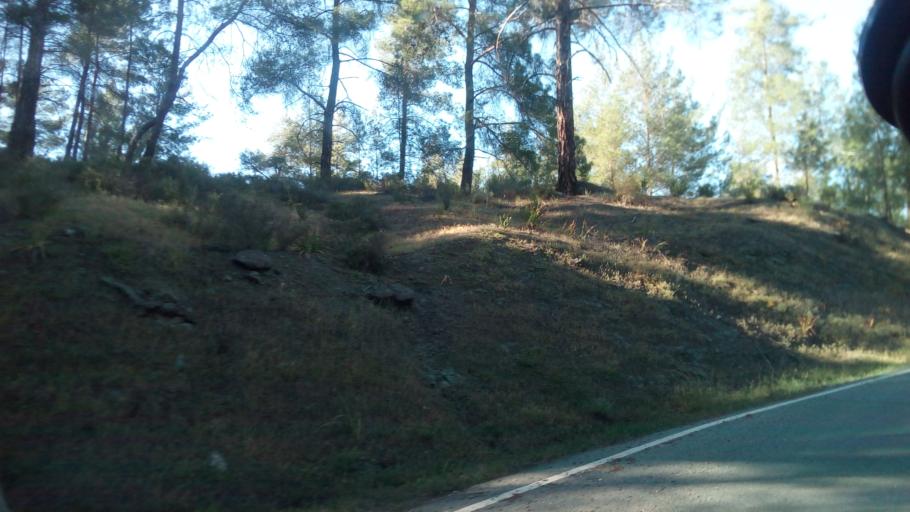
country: CY
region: Limassol
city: Pachna
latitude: 34.8848
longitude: 32.7541
